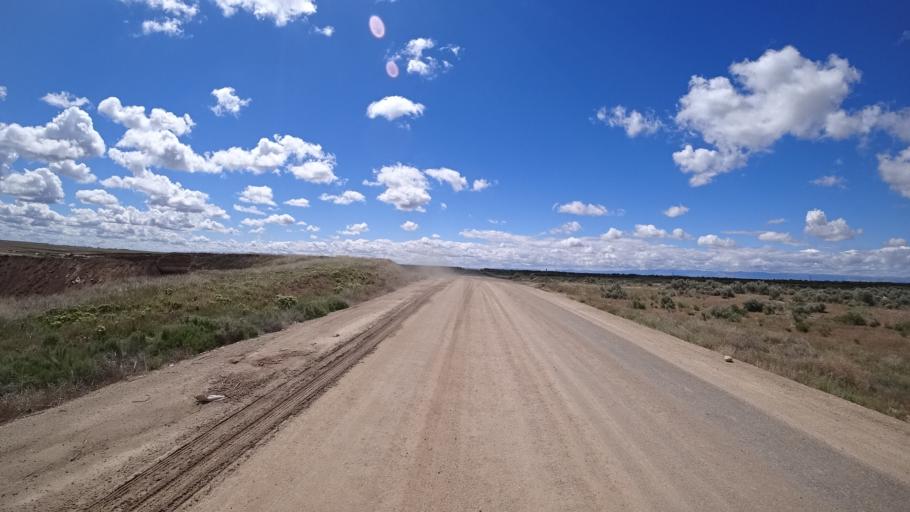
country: US
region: Idaho
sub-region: Ada County
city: Garden City
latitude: 43.4854
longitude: -116.2743
